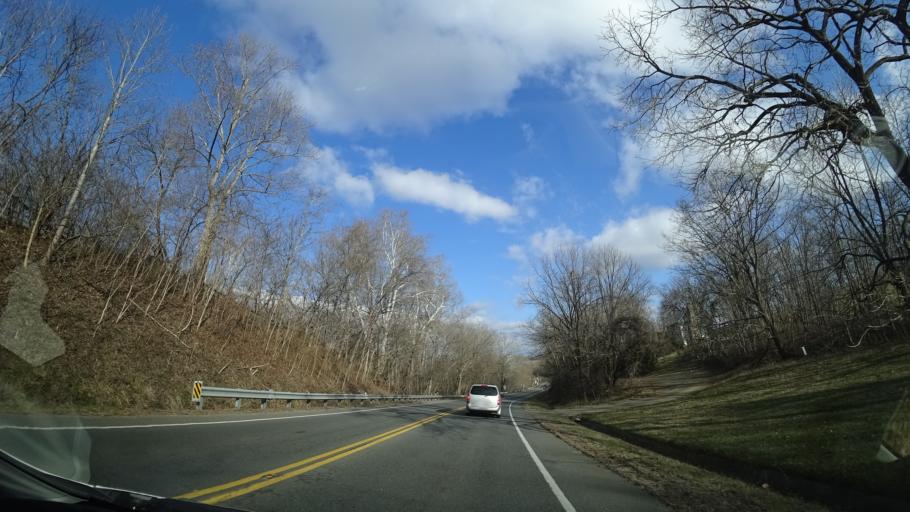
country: US
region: Virginia
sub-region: Fauquier County
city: Marshall
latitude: 38.9126
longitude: -77.9214
